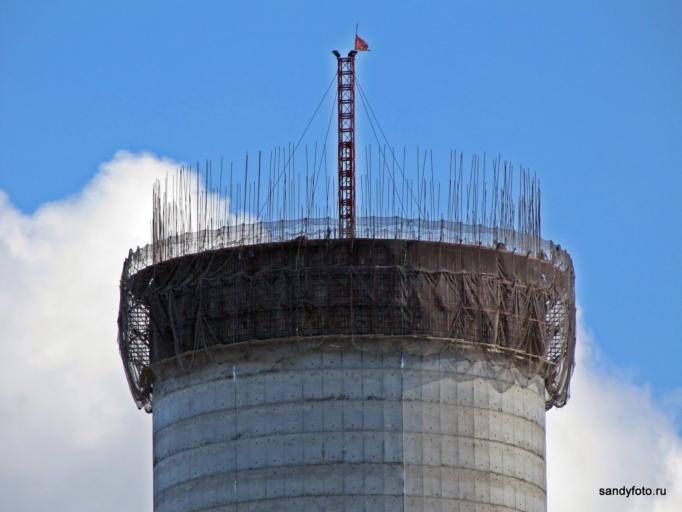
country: RU
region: Chelyabinsk
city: Bobrovka
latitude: 54.0408
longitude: 61.6582
